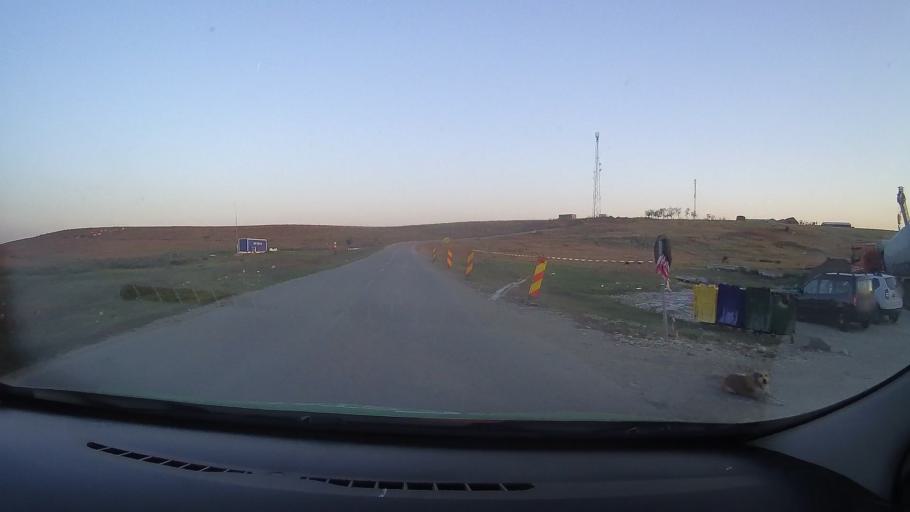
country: RO
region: Timis
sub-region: Comuna Manastiur
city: Manastiur
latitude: 45.8268
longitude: 22.0705
